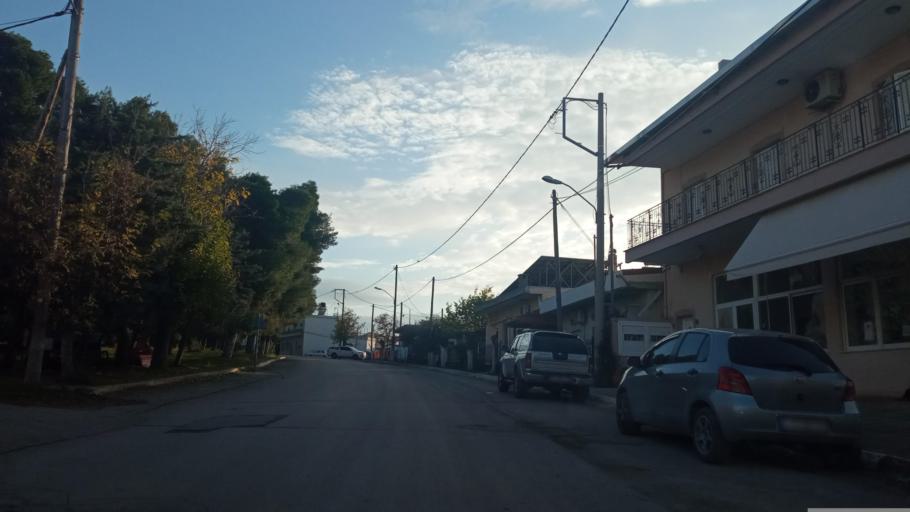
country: GR
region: Central Greece
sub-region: Nomos Evvoias
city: Psachna
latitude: 38.5834
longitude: 23.7133
